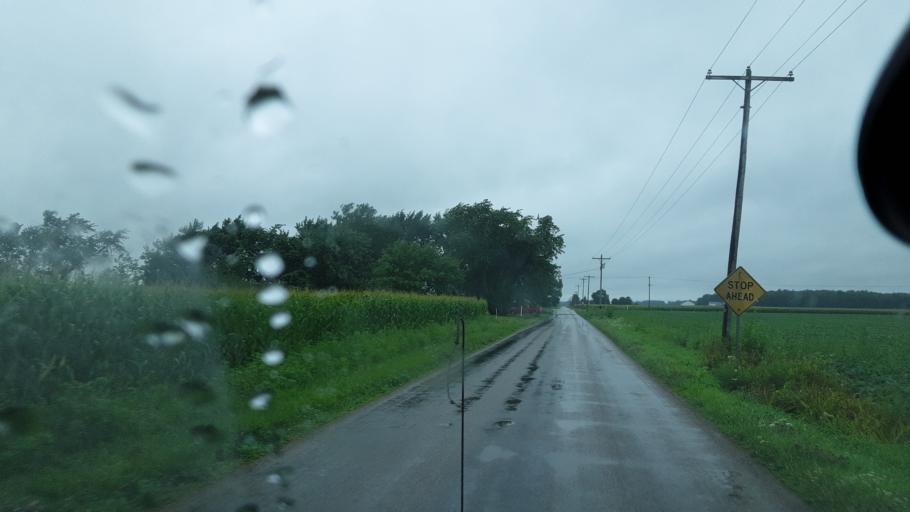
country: US
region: Indiana
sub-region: Adams County
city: Decatur
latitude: 40.7439
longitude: -84.8558
